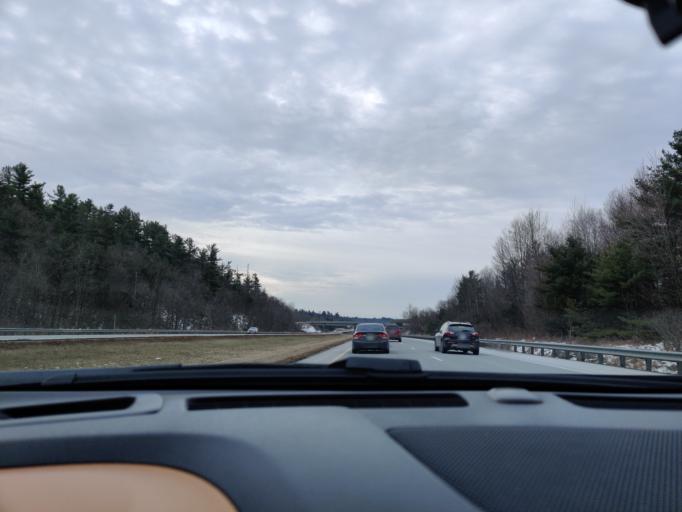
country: US
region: New York
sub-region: Jefferson County
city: Alexandria Bay
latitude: 44.4476
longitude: -75.8902
